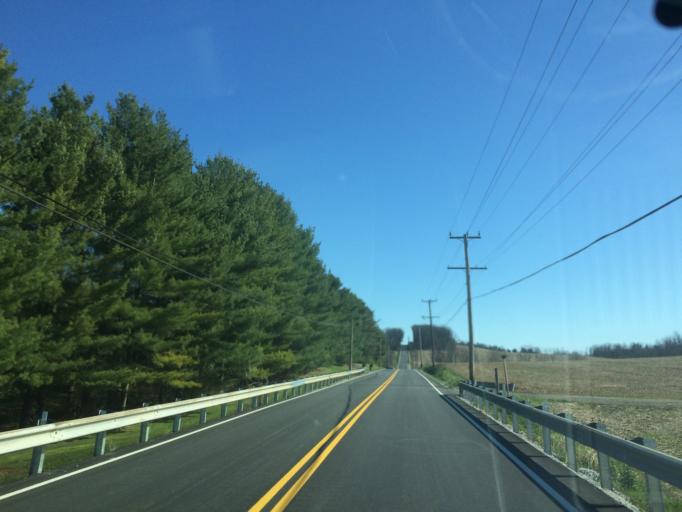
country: US
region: Maryland
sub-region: Carroll County
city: Westminster
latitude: 39.6361
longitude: -76.9863
